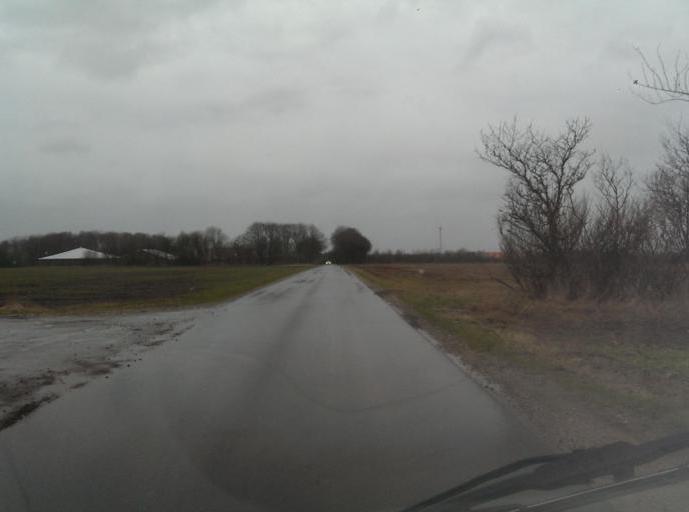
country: DK
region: Central Jutland
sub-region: Ringkobing-Skjern Kommune
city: Skjern
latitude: 56.0517
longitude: 8.4416
